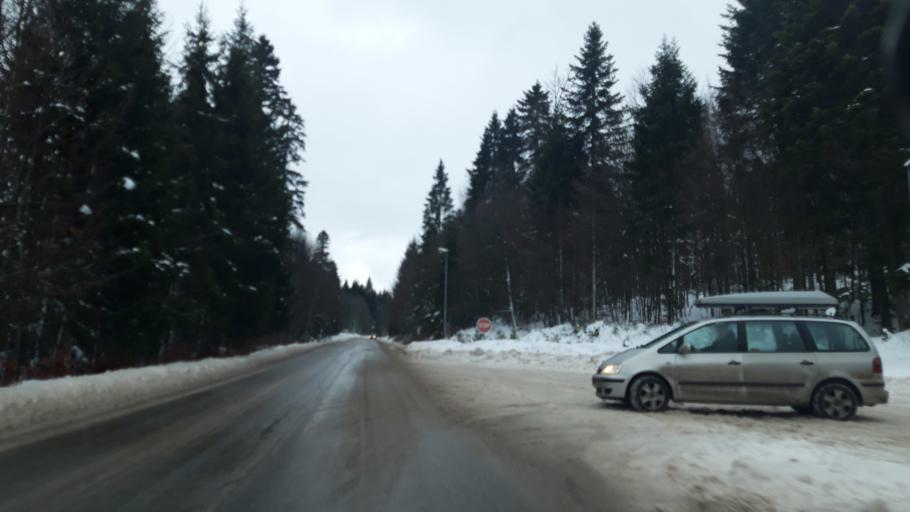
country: BA
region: Republika Srpska
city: Han Pijesak
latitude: 44.0685
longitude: 18.9456
